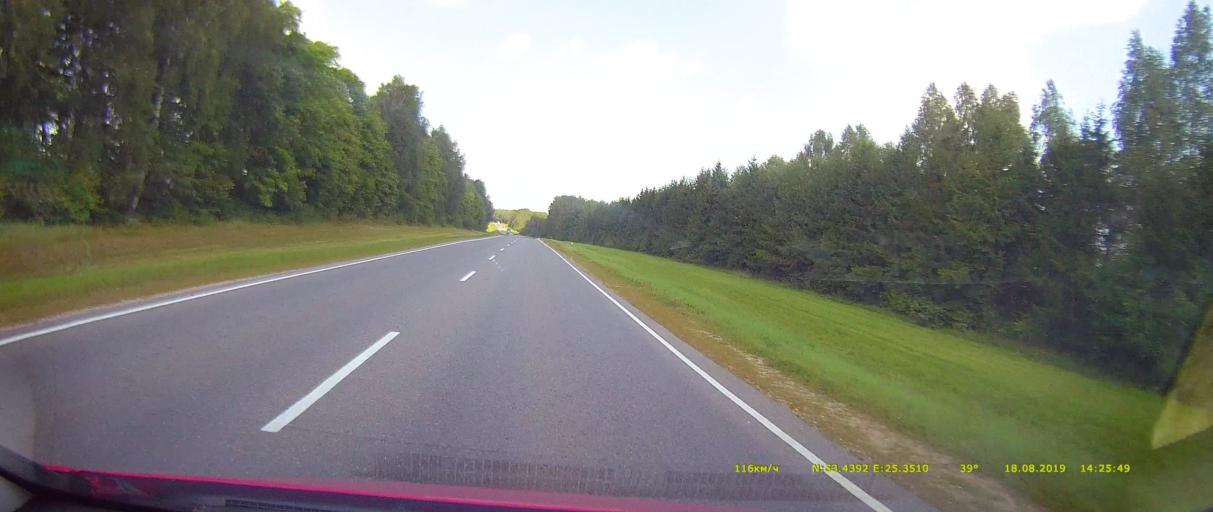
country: BY
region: Grodnenskaya
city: Dzyatlava
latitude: 53.4527
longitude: 25.3637
